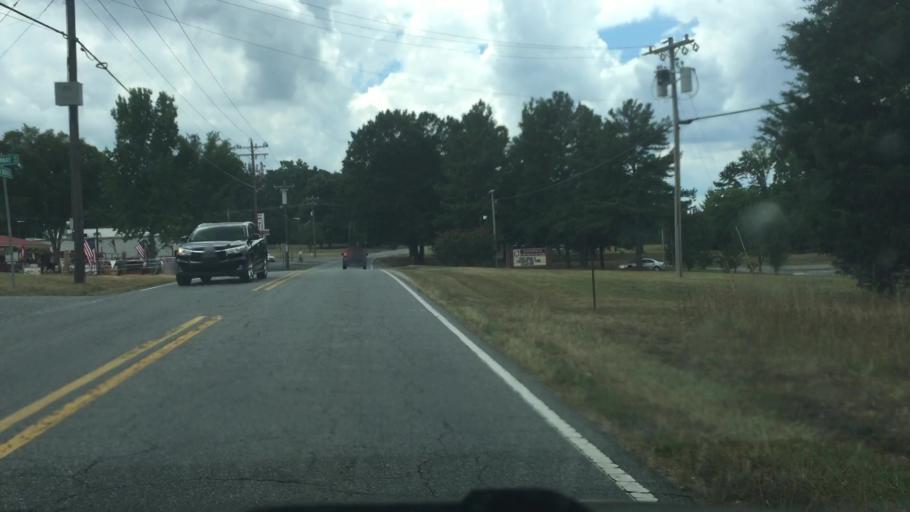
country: US
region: North Carolina
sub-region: Rowan County
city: Enochville
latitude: 35.5179
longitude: -80.6700
